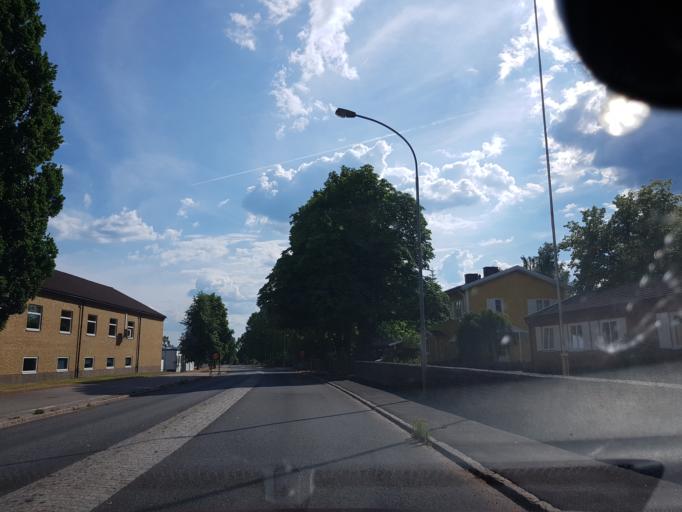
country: SE
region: Joenkoeping
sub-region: Gislaveds Kommun
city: Gislaved
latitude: 57.2981
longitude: 13.5299
